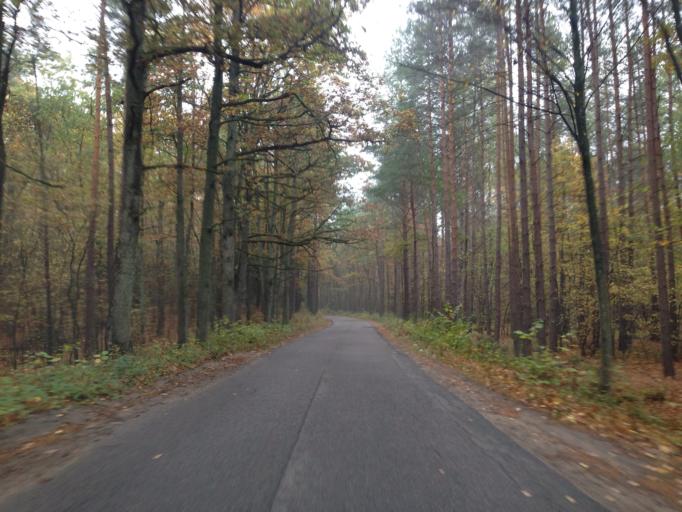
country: PL
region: Warmian-Masurian Voivodeship
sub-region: Powiat dzialdowski
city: Lidzbark
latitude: 53.2491
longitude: 19.7444
